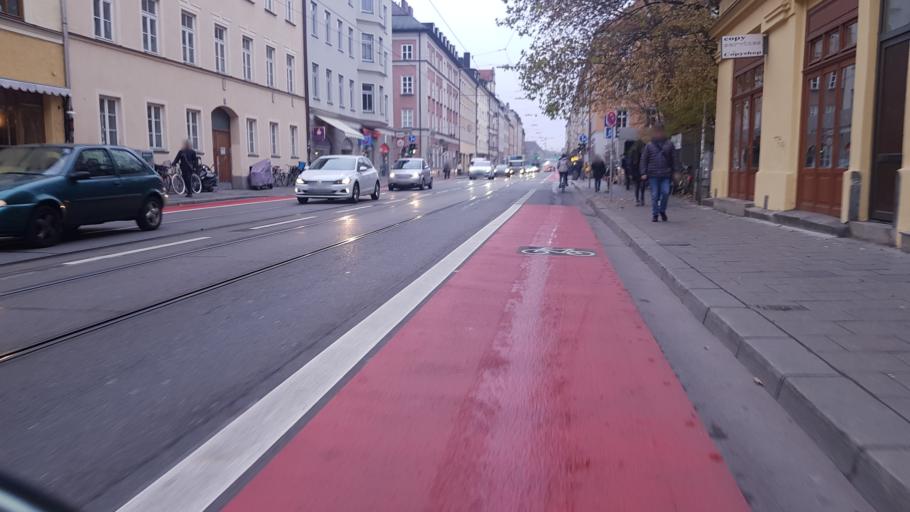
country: DE
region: Bavaria
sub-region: Upper Bavaria
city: Munich
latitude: 48.1305
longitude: 11.5726
